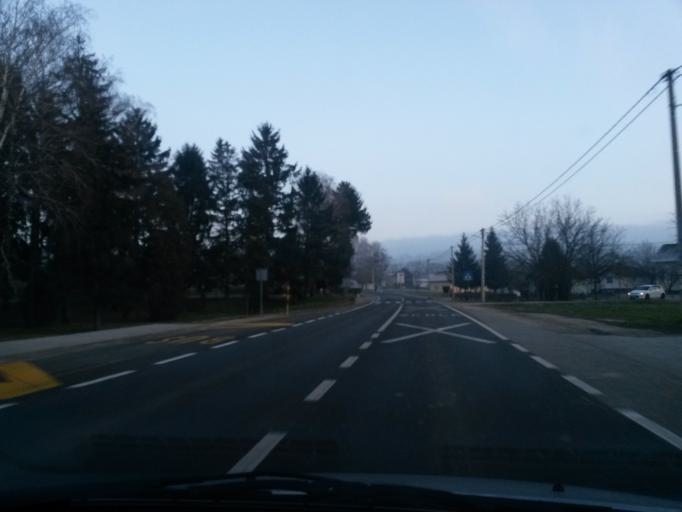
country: HR
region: Koprivnicko-Krizevacka
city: Reka
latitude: 46.1896
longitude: 16.7436
